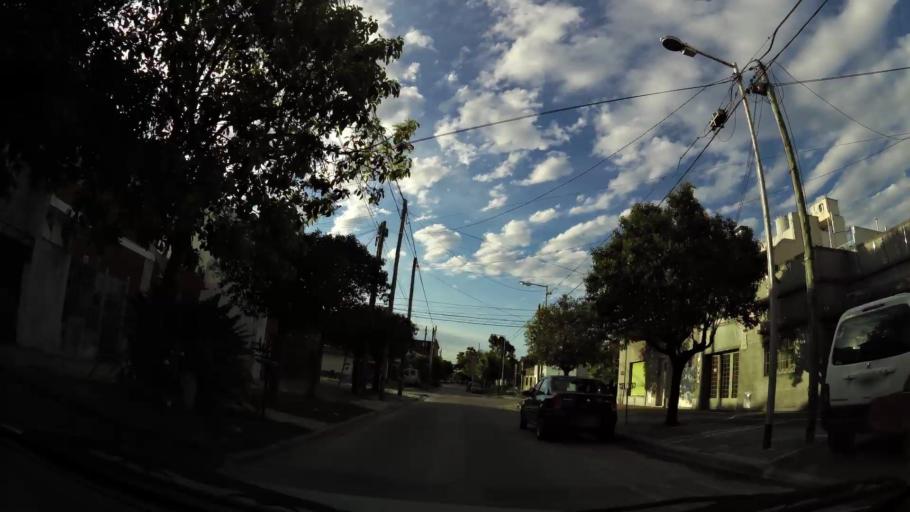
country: AR
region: Buenos Aires
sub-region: Partido de Avellaneda
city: Avellaneda
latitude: -34.6886
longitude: -58.3478
